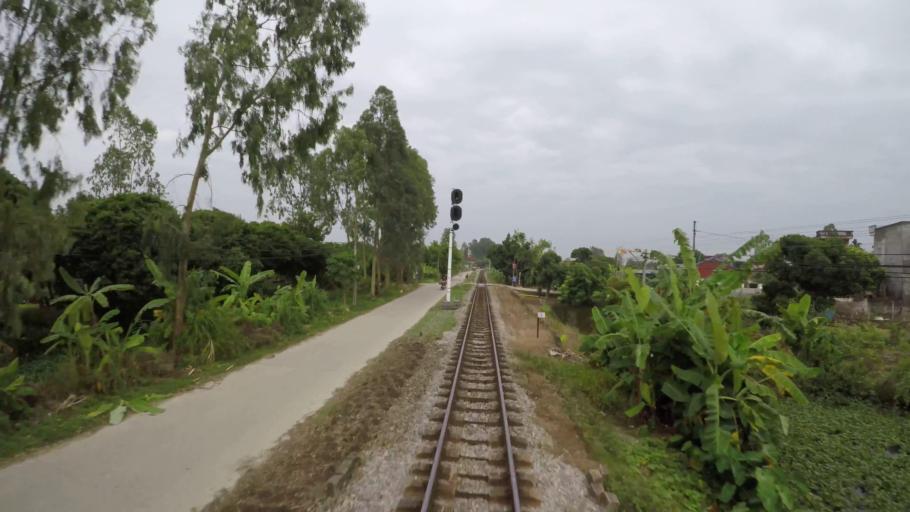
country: VN
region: Hai Duong
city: Lai Cach
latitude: 20.9493
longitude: 106.2487
